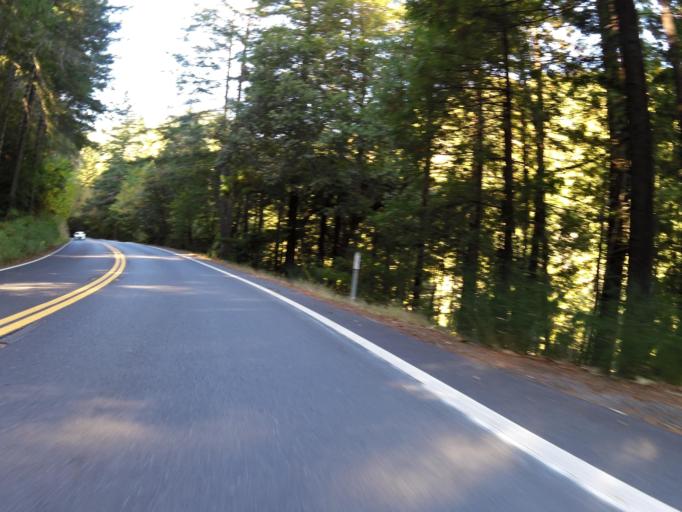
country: US
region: California
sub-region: Humboldt County
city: Redway
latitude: 39.8662
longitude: -123.7182
